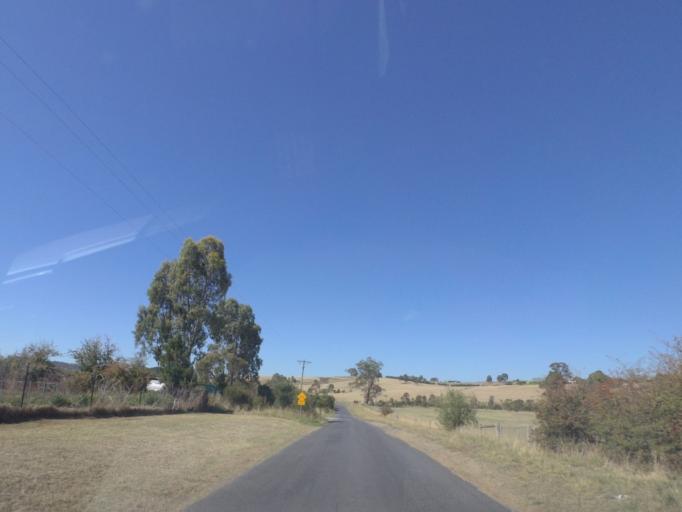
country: AU
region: Victoria
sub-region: Yarra Ranges
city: Chirnside Park
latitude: -37.7295
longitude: 145.2889
